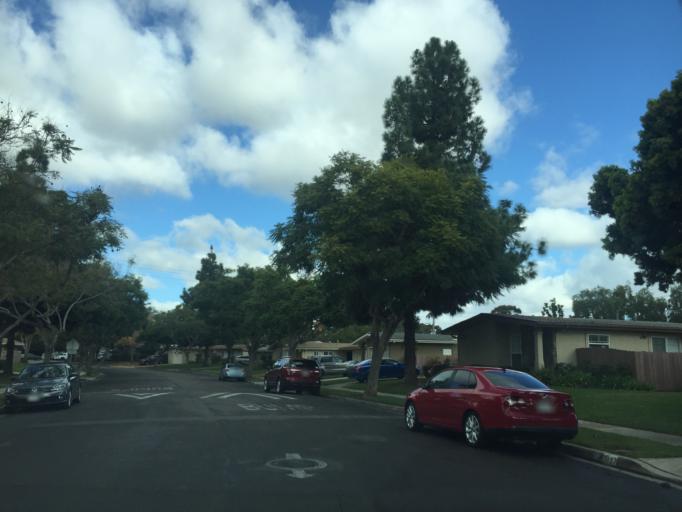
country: US
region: California
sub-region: San Diego County
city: La Jolla
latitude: 32.8035
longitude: -117.2238
